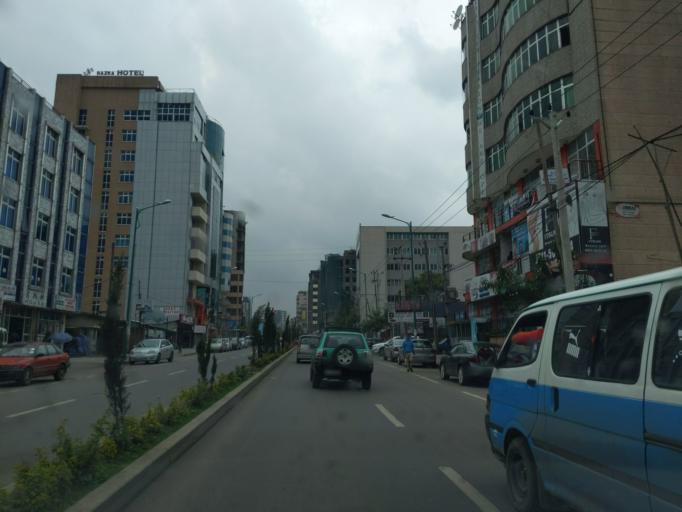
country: ET
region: Adis Abeba
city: Addis Ababa
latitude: 8.9924
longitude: 38.7663
